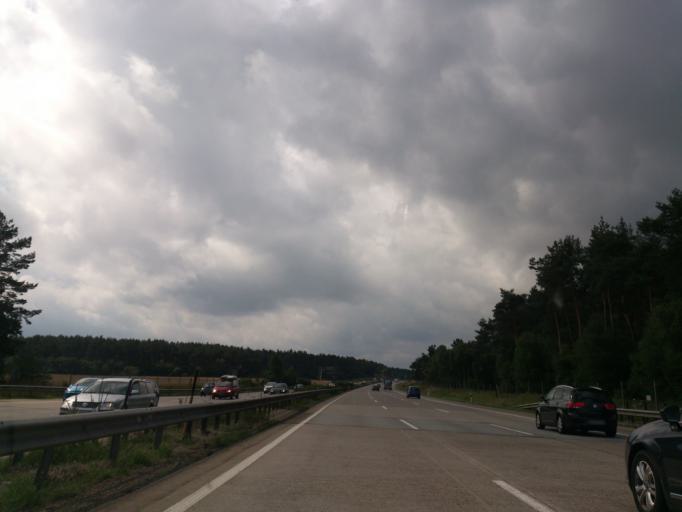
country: DE
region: Lower Saxony
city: Egestorf
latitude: 53.1823
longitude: 10.0823
